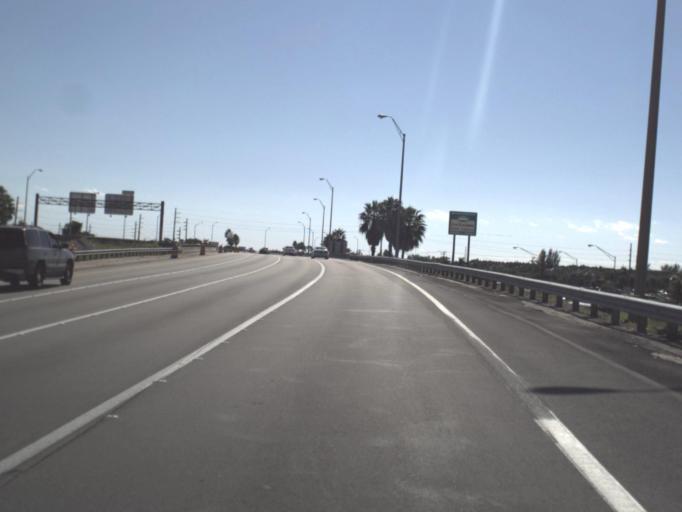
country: US
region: Florida
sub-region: Miami-Dade County
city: Richmond Heights
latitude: 25.6310
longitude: -80.3836
